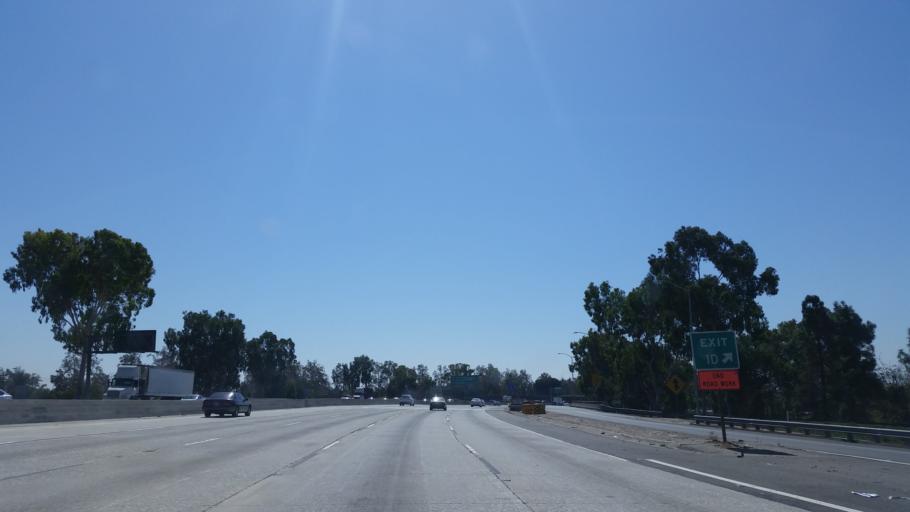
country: US
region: California
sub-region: Orange County
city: Los Alamitos
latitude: 33.8044
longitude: -118.0816
